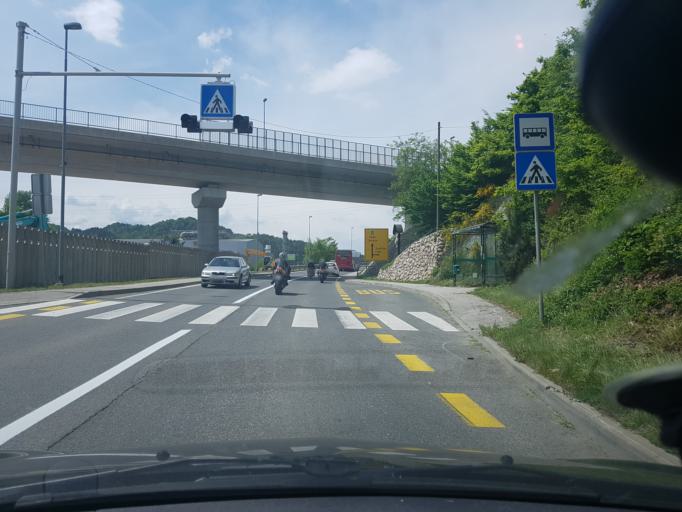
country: SI
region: Store
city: Store
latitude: 46.2244
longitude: 15.3112
